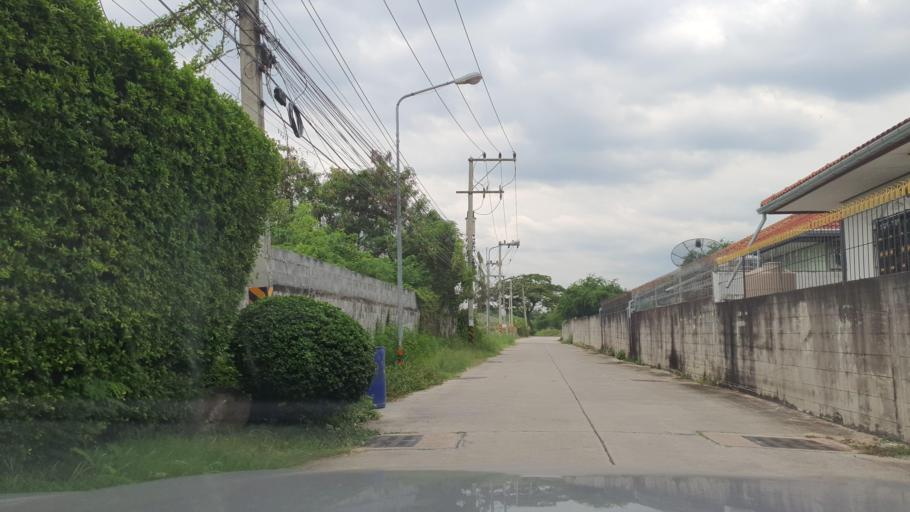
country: TH
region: Chon Buri
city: Phatthaya
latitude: 12.8820
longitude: 100.8926
